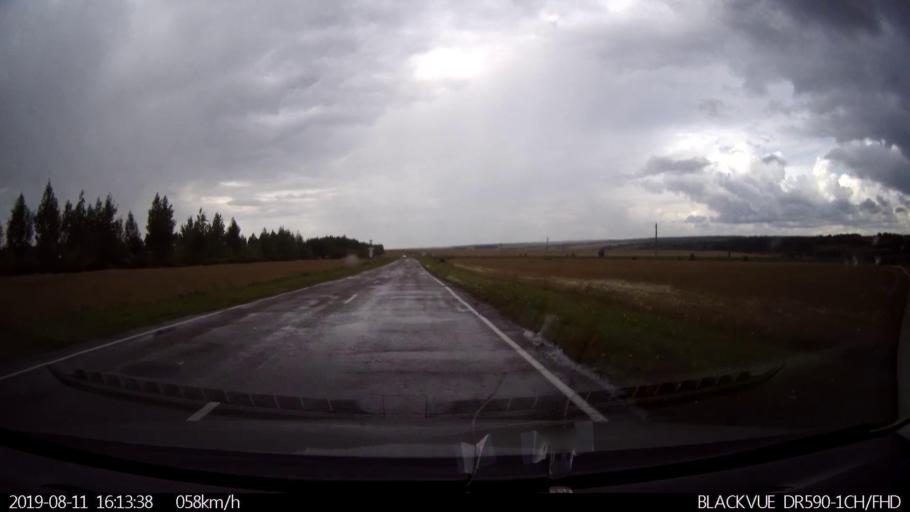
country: RU
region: Ulyanovsk
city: Ignatovka
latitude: 54.0217
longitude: 47.6363
